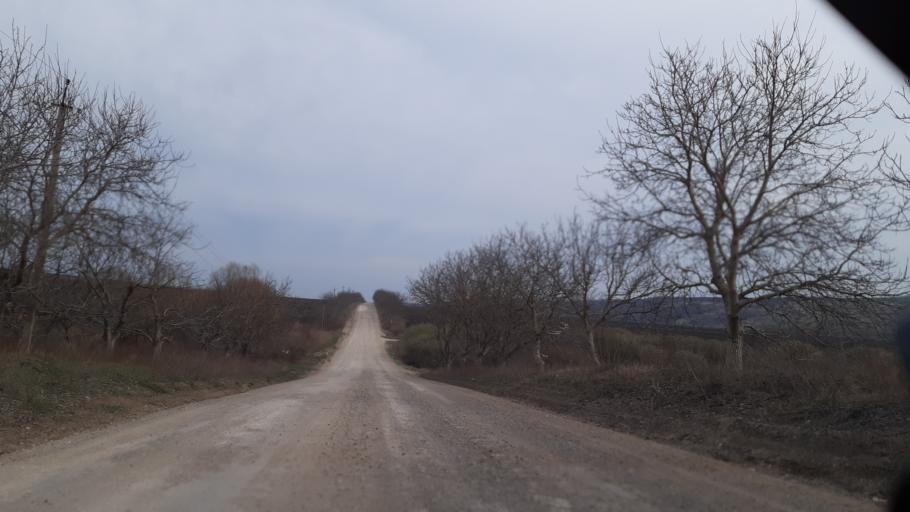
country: MD
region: Soldanesti
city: Soldanesti
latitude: 47.6980
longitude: 28.7275
